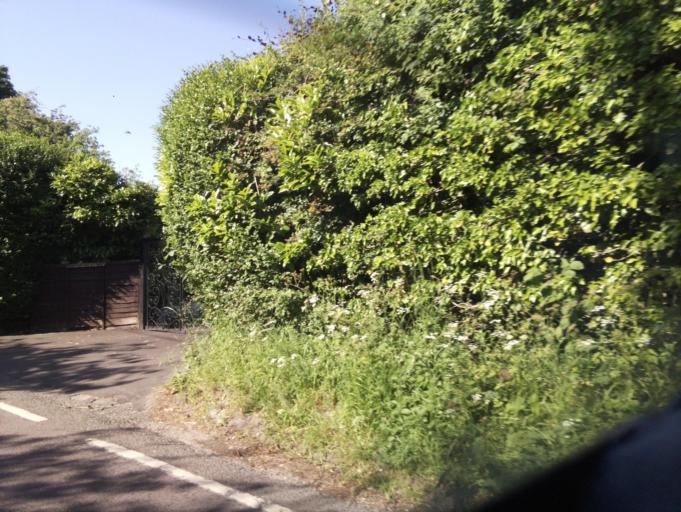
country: GB
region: England
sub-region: Hampshire
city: Winchester
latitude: 51.0840
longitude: -1.3464
